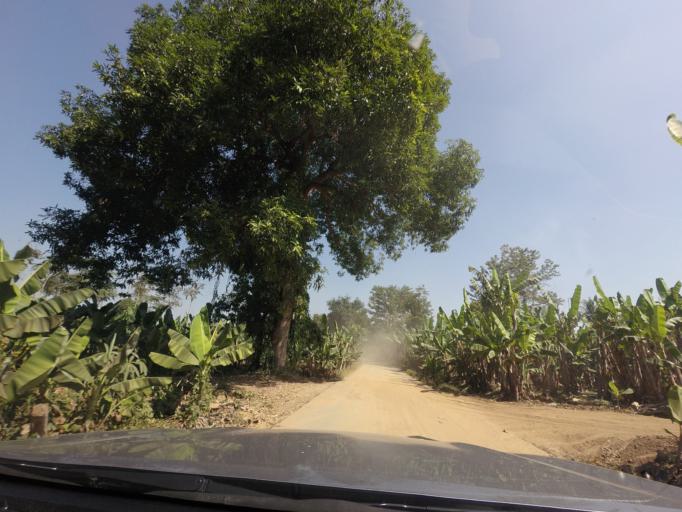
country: TH
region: Sukhothai
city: Sawankhalok
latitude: 17.2780
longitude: 99.8280
